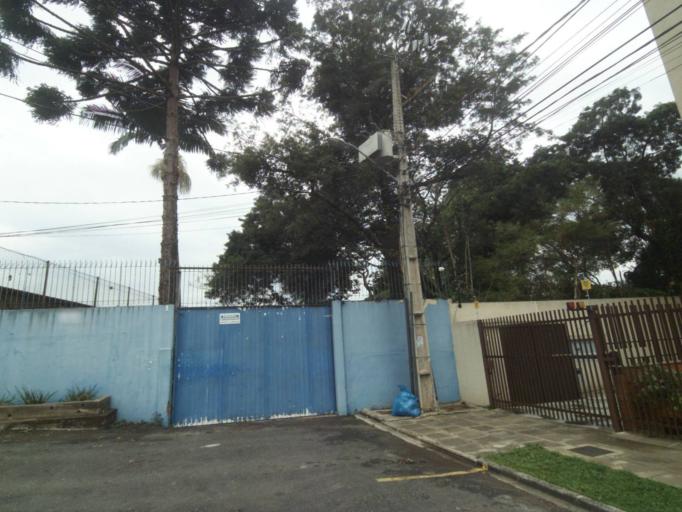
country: BR
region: Parana
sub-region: Curitiba
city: Curitiba
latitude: -25.4727
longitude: -49.3017
